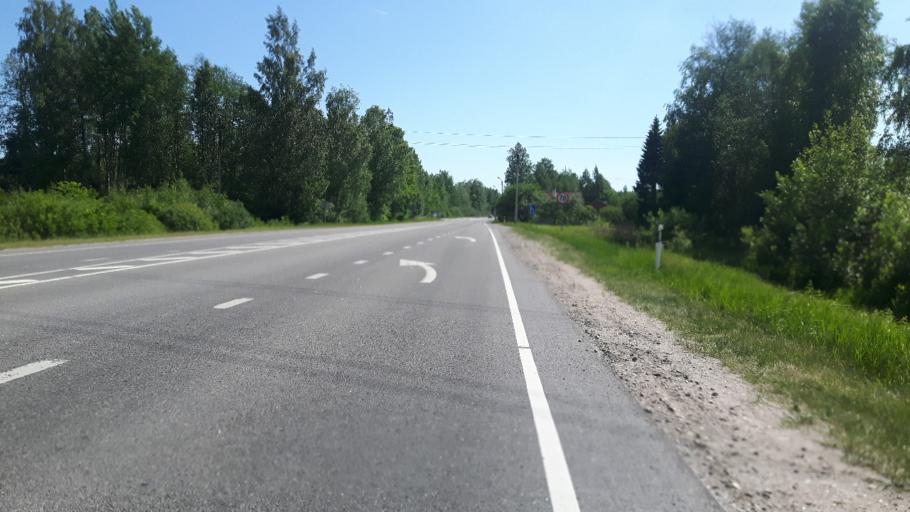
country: EE
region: Paernumaa
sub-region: Paikuse vald
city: Paikuse
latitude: 58.3896
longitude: 24.6411
